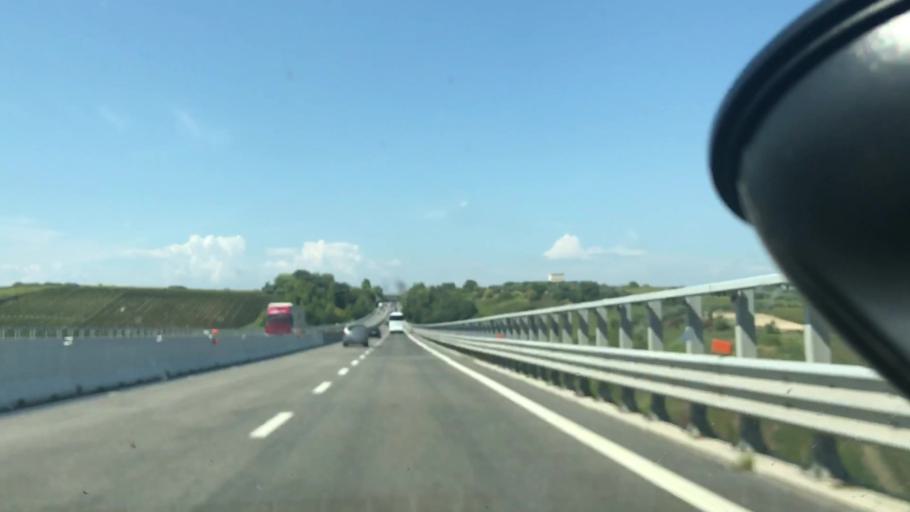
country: IT
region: Abruzzo
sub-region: Provincia di Chieti
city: Marina di San Vito
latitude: 42.3128
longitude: 14.4161
